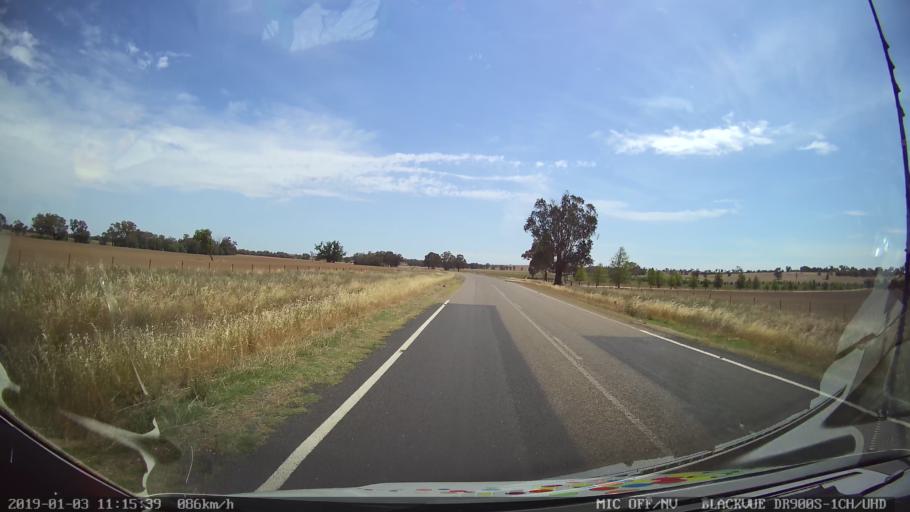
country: AU
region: New South Wales
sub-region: Young
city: Young
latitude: -34.1615
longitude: 148.2665
